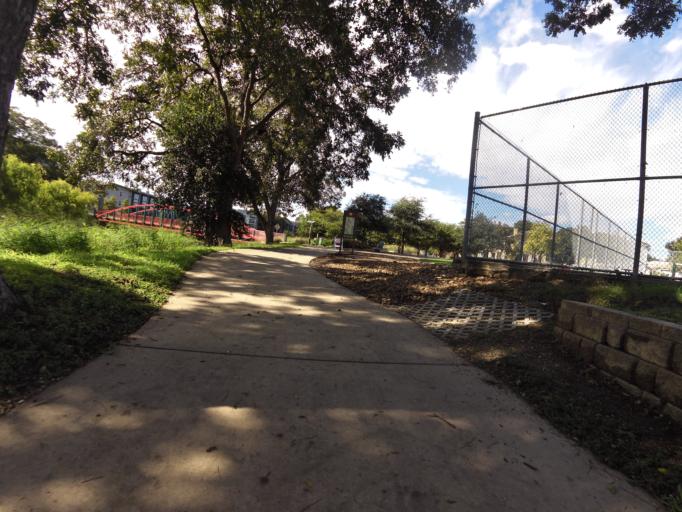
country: US
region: Texas
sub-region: Bexar County
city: San Antonio
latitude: 29.4044
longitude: -98.4898
